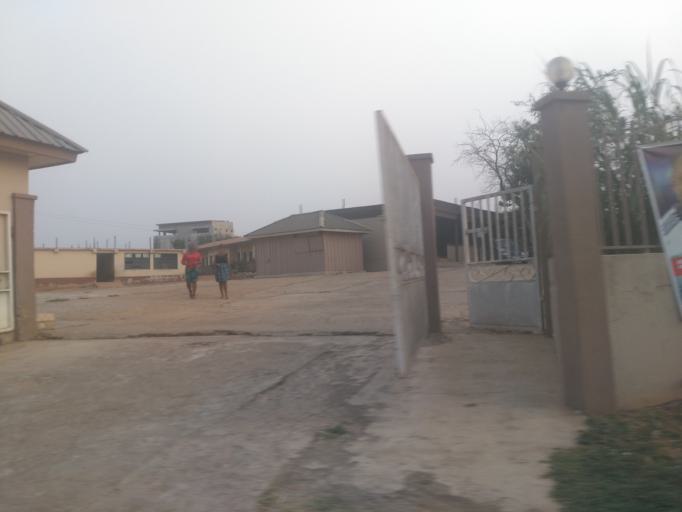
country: GH
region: Ashanti
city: Kumasi
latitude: 6.6705
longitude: -1.6048
